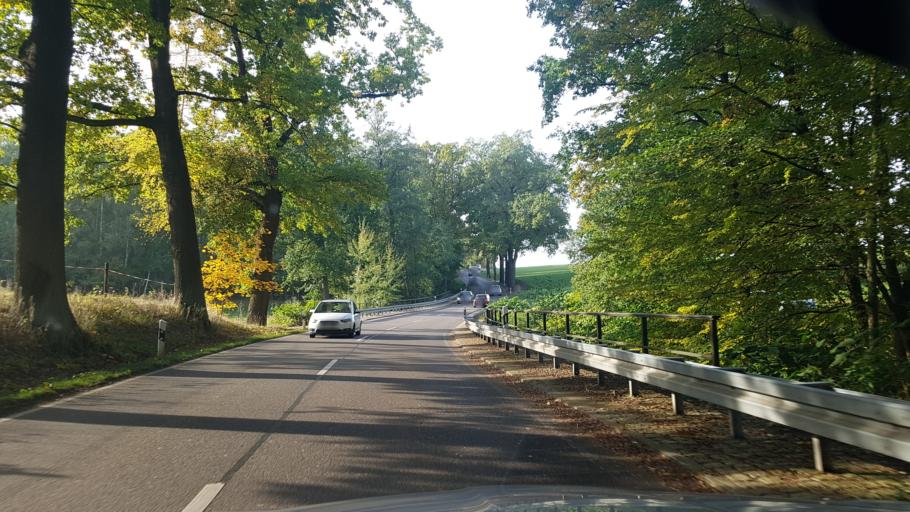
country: DE
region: Saxony
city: Struppen
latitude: 50.9271
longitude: 14.0359
